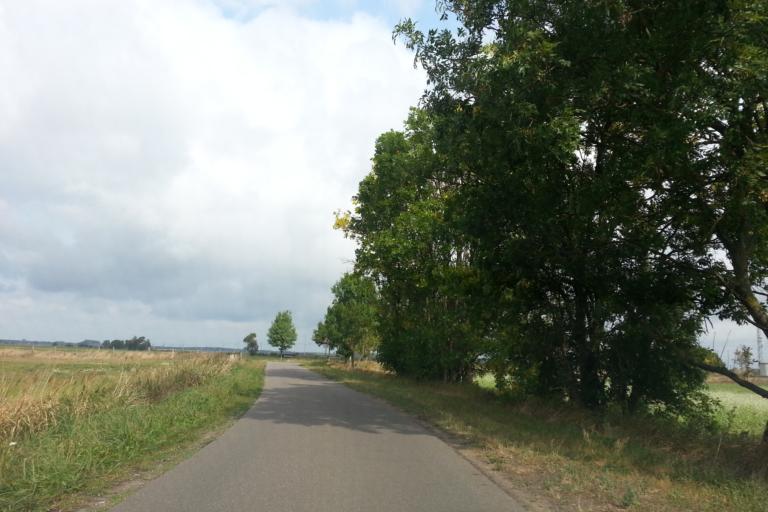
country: DE
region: Mecklenburg-Vorpommern
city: Ferdinandshof
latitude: 53.6663
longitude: 13.8732
